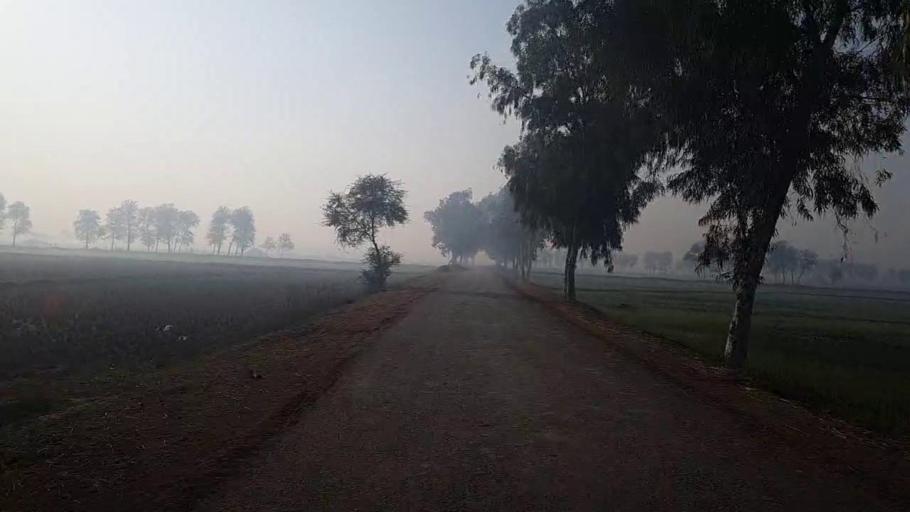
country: PK
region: Sindh
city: Mehar
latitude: 27.1423
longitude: 67.8229
